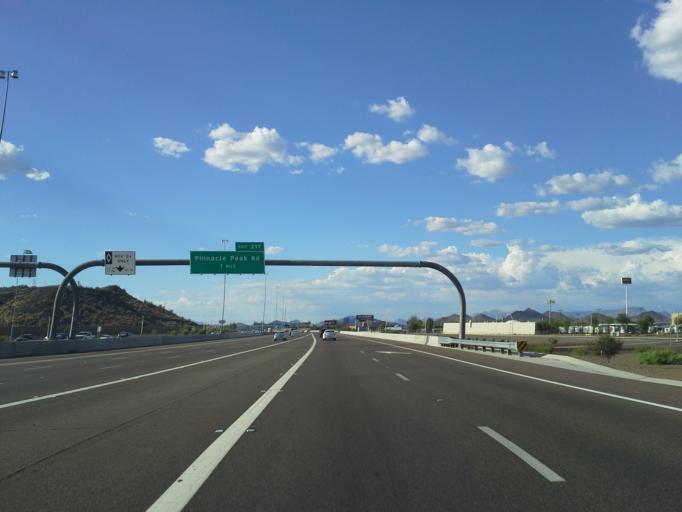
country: US
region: Arizona
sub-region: Maricopa County
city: Peoria
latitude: 33.6819
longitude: -112.1122
